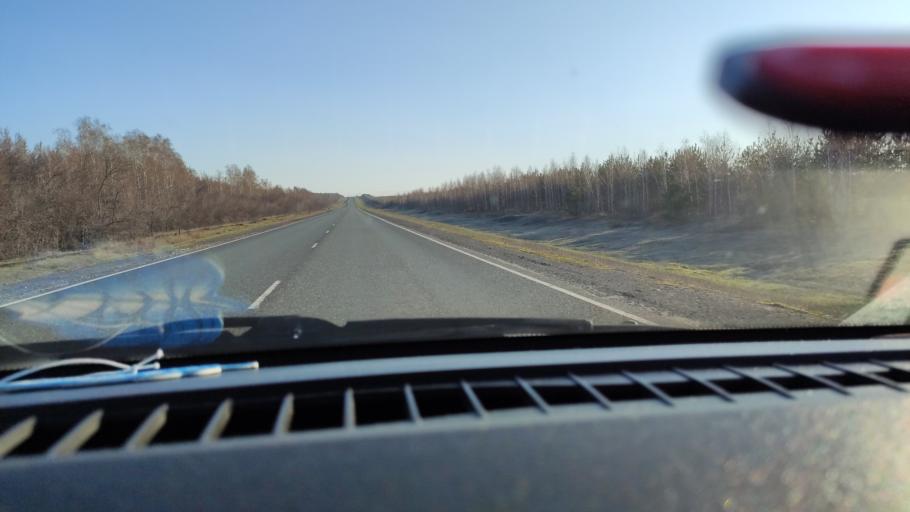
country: RU
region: Saratov
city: Balakovo
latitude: 52.1461
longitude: 47.8067
